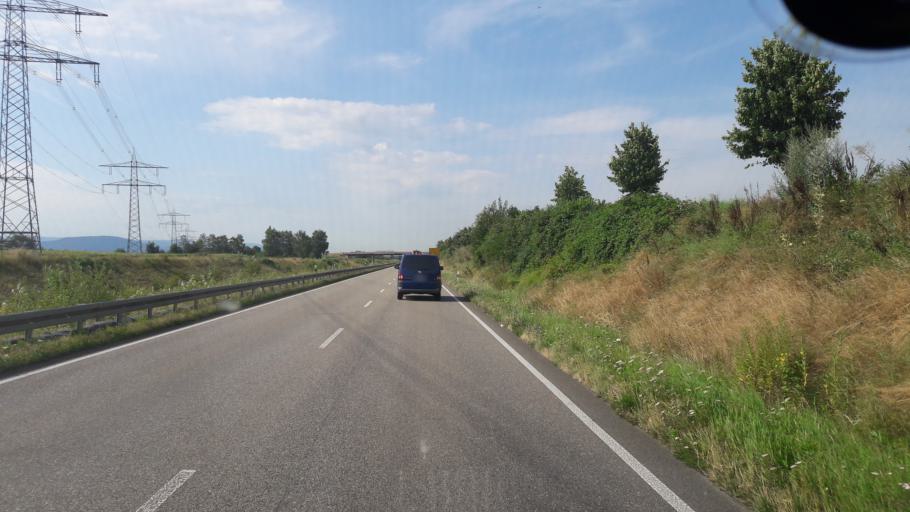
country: DE
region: Baden-Wuerttemberg
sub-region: Karlsruhe Region
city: Bietigheim
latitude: 48.9042
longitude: 8.2605
